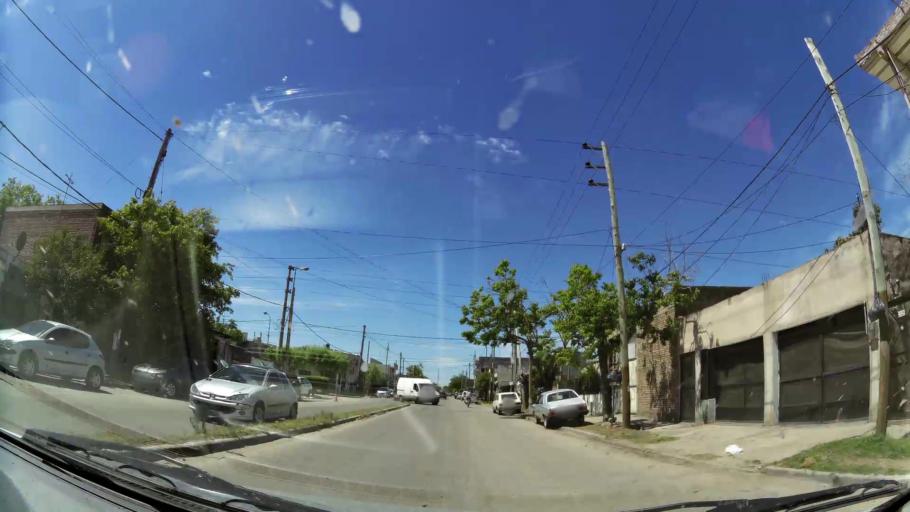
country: AR
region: Buenos Aires
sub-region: Partido de Quilmes
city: Quilmes
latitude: -34.7327
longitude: -58.3075
